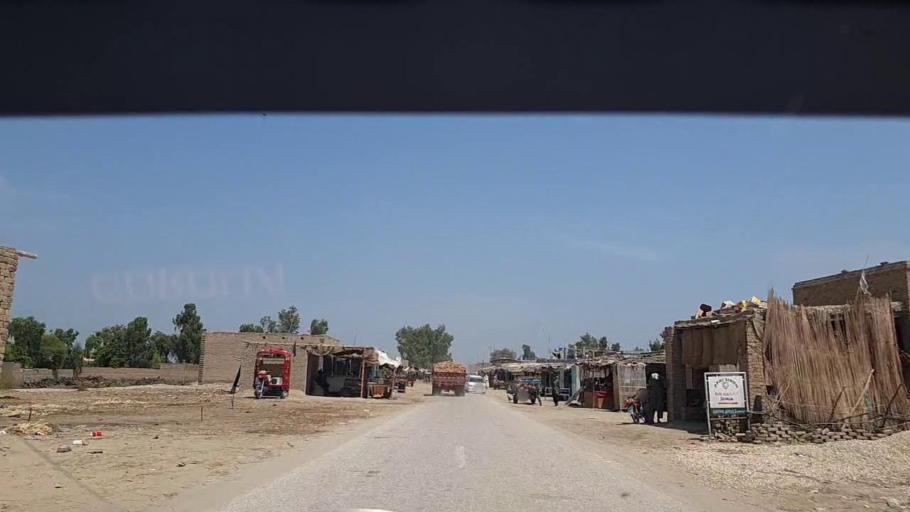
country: PK
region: Sindh
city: Thul
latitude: 28.1190
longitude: 68.8133
